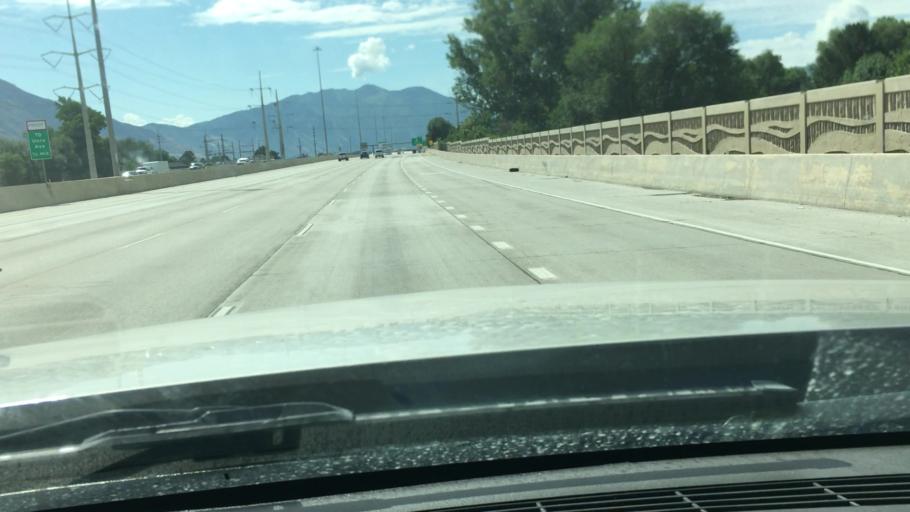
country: US
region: Utah
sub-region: Utah County
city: Provo
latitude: 40.2406
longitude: -111.6918
